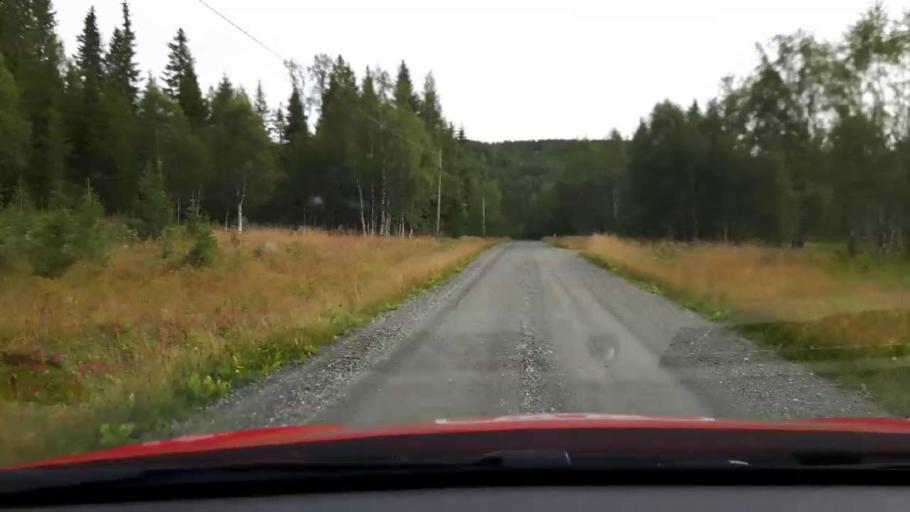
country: SE
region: Jaemtland
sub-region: Are Kommun
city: Are
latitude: 63.7718
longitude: 13.0830
